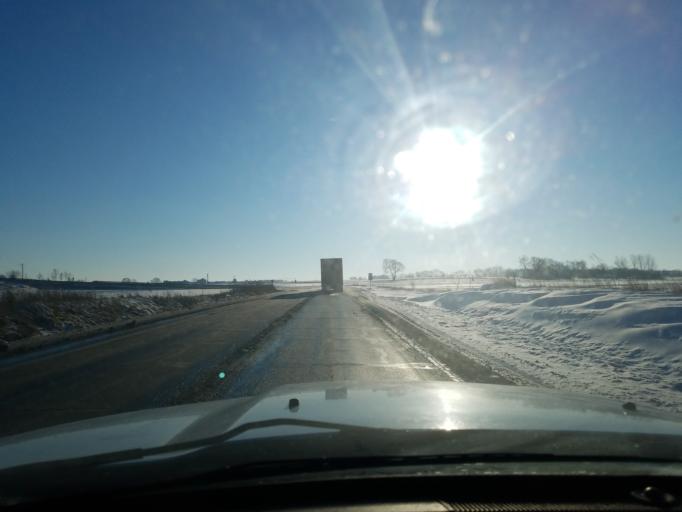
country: US
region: Indiana
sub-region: Noble County
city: Rome City
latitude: 41.4525
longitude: -85.4086
